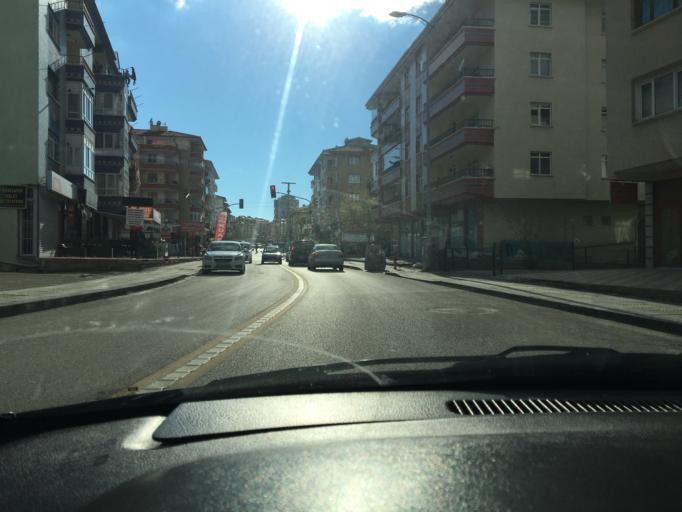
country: TR
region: Ankara
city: Etimesgut
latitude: 39.9485
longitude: 32.5702
